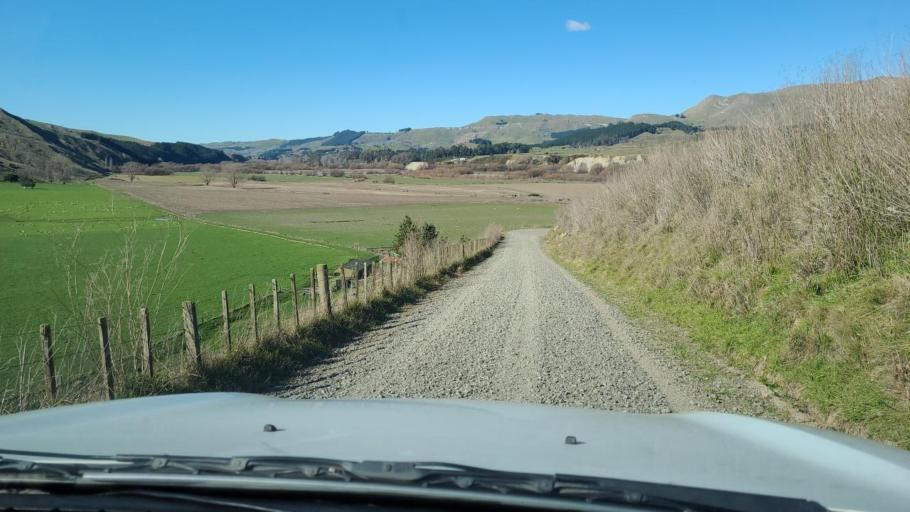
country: NZ
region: Hawke's Bay
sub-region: Hastings District
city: Hastings
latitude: -39.7628
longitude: 176.8094
